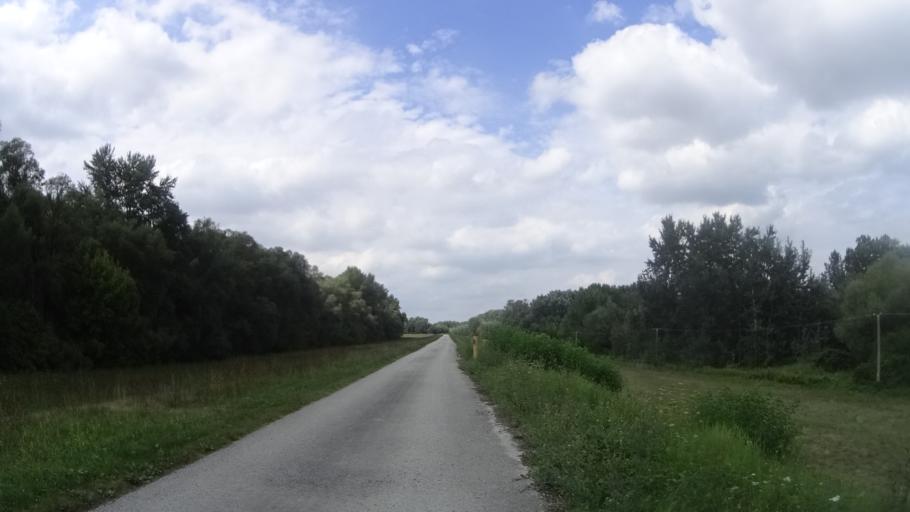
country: SK
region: Trnavsky
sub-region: Okres Dunajska Streda
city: Velky Meder
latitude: 47.7857
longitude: 17.6941
